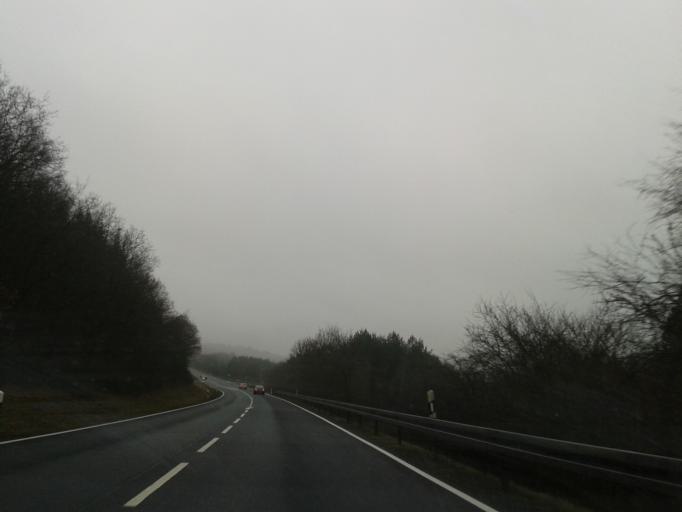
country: DE
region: Bavaria
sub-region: Regierungsbezirk Unterfranken
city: Burgpreppach
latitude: 50.1340
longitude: 10.6044
